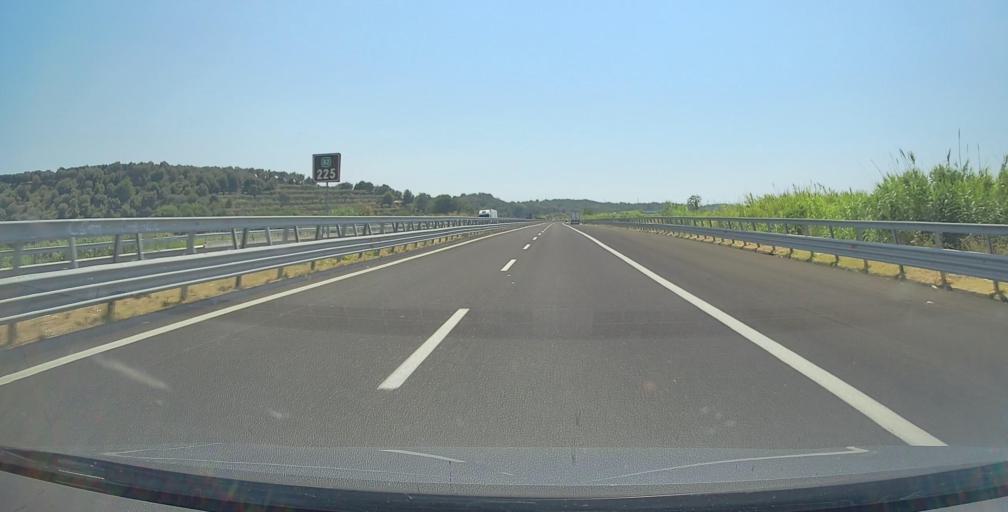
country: IT
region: Calabria
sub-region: Provincia di Reggio Calabria
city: Laureana di Borrello
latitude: 38.5041
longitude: 16.0354
